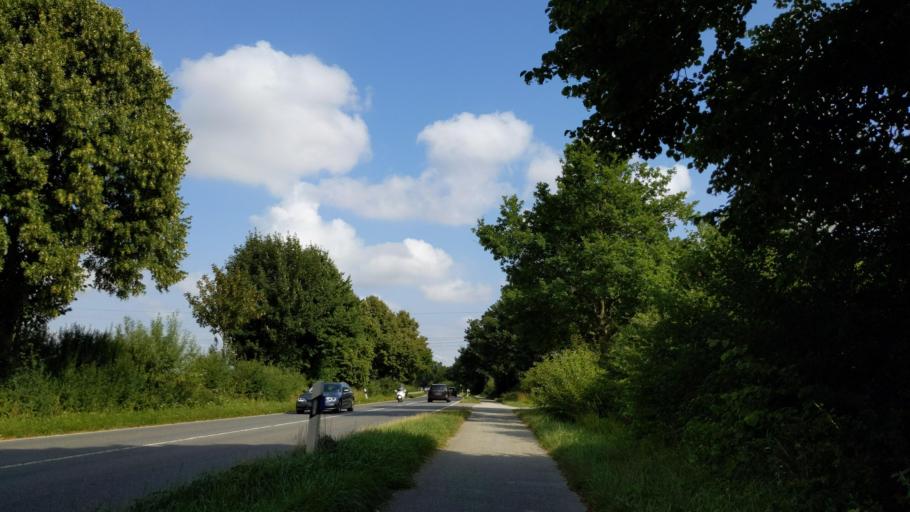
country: DE
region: Schleswig-Holstein
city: Stockelsdorf
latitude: 53.9184
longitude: 10.6397
